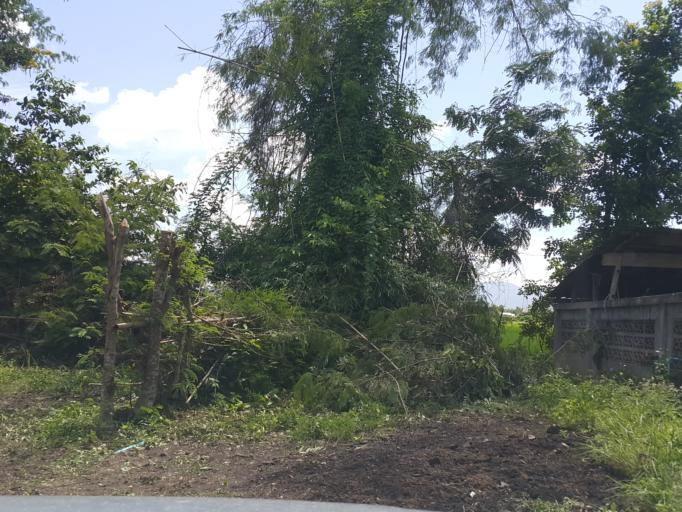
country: TH
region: Chiang Mai
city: San Kamphaeng
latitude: 18.6991
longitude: 99.1067
